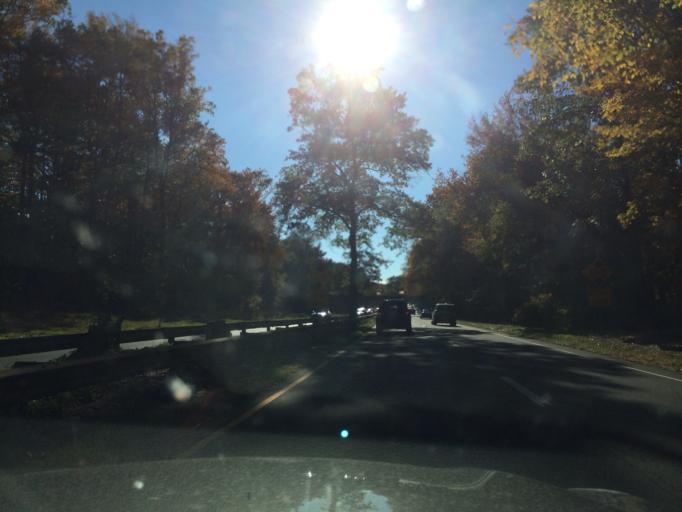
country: US
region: Connecticut
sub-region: Fairfield County
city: Norwalk
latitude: 41.1544
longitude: -73.4019
